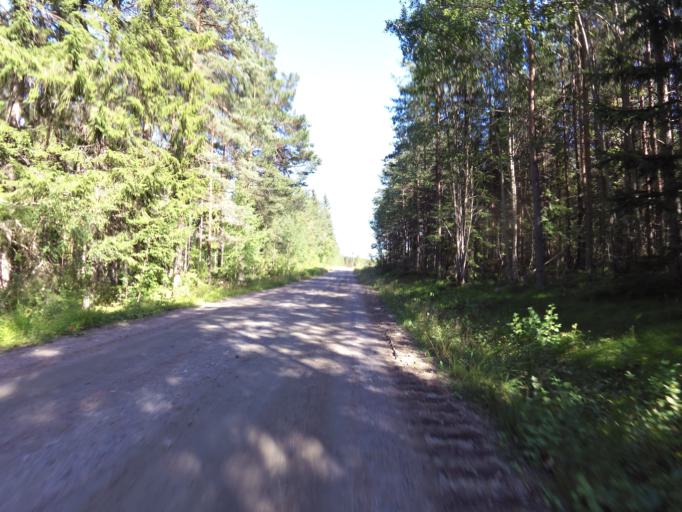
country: SE
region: Gaevleborg
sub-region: Hofors Kommun
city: Hofors
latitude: 60.5080
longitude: 16.3910
